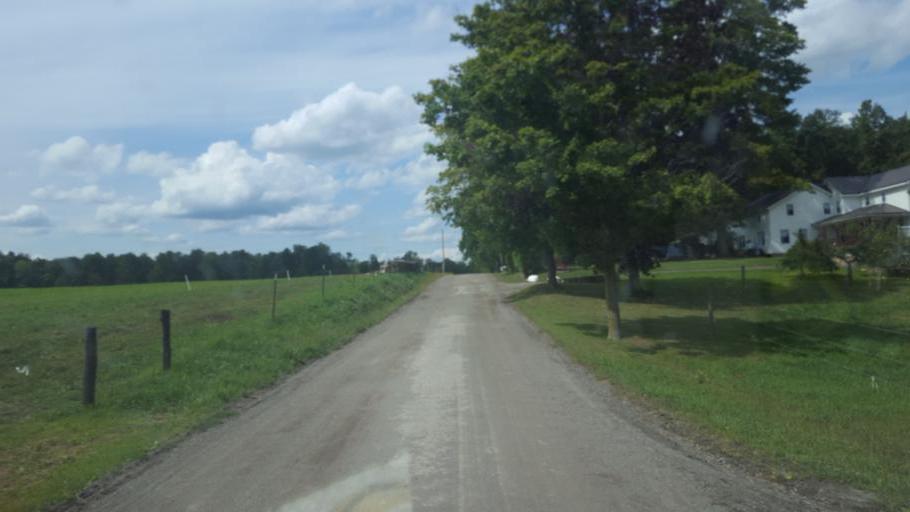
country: US
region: Ohio
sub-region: Geauga County
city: Middlefield
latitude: 41.4259
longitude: -80.9876
